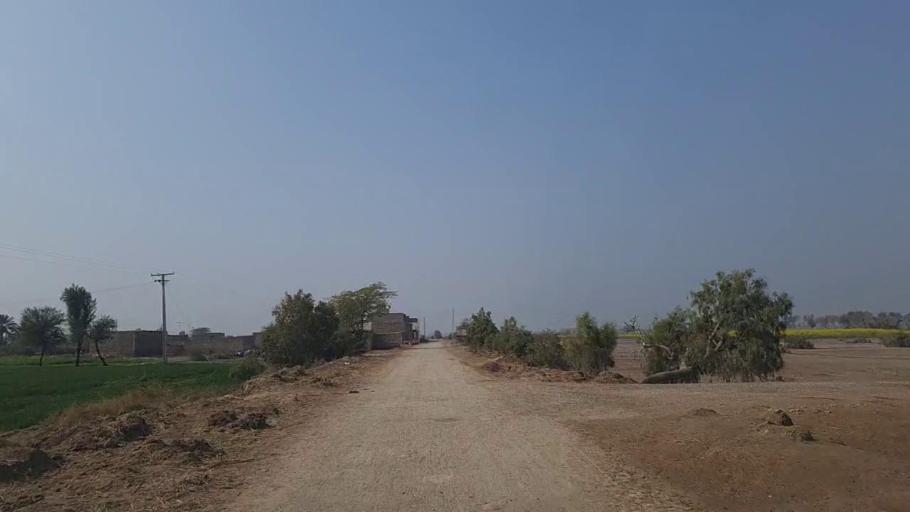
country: PK
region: Sindh
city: Nawabshah
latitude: 26.3601
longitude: 68.4232
